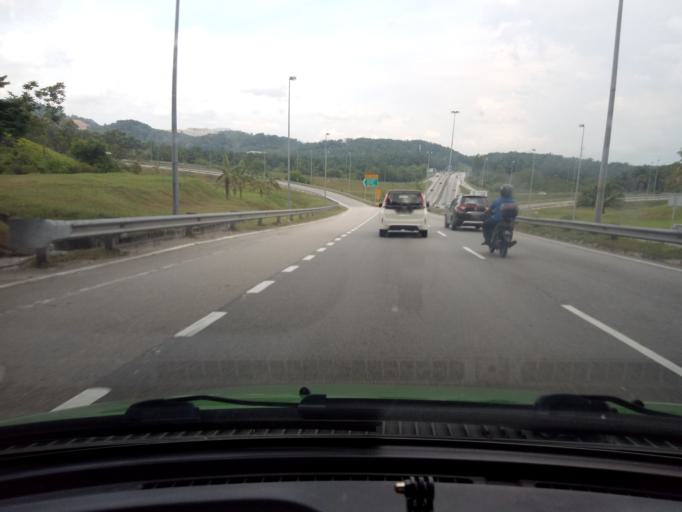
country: MY
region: Selangor
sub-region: Hulu Langat
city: Semenyih
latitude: 2.9858
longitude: 101.8277
